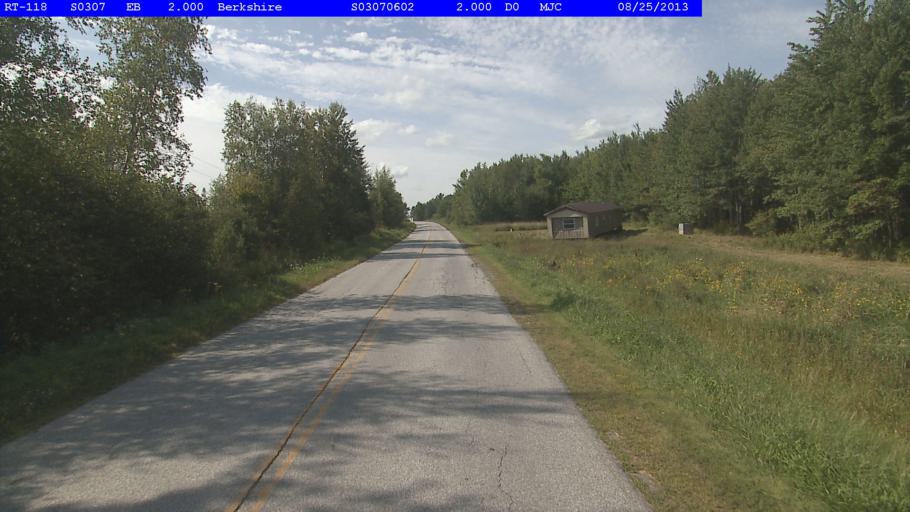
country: US
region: Vermont
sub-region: Franklin County
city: Enosburg Falls
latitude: 44.9478
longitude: -72.7439
